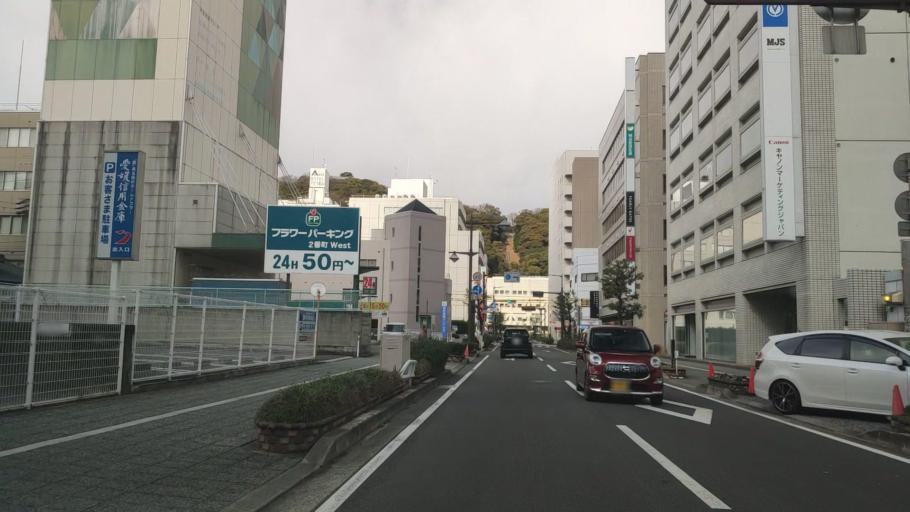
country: JP
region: Ehime
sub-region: Shikoku-chuo Shi
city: Matsuyama
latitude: 33.8394
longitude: 132.7680
